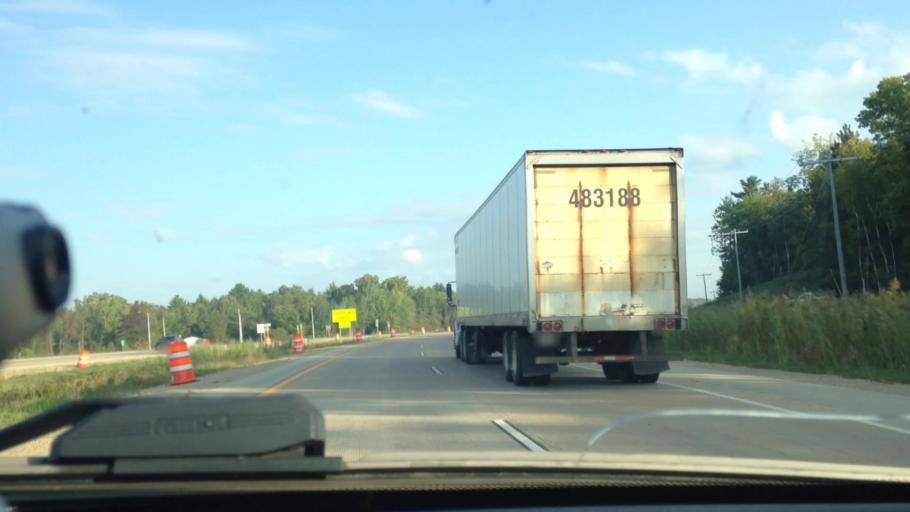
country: US
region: Wisconsin
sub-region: Oconto County
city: Oconto Falls
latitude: 44.7942
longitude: -88.0490
